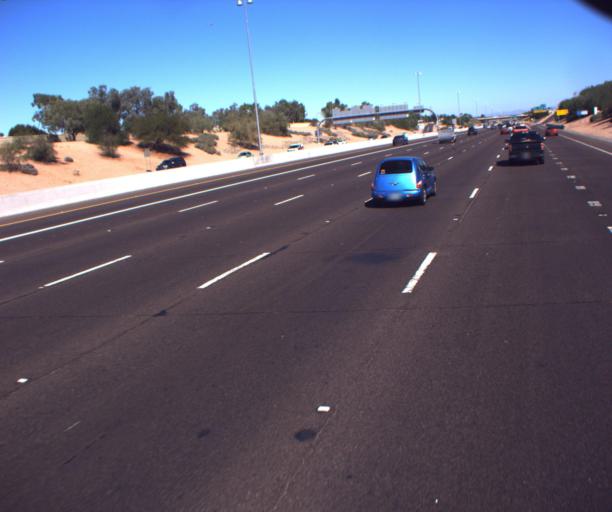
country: US
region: Arizona
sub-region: Maricopa County
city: Tempe
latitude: 33.3994
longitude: -111.8909
